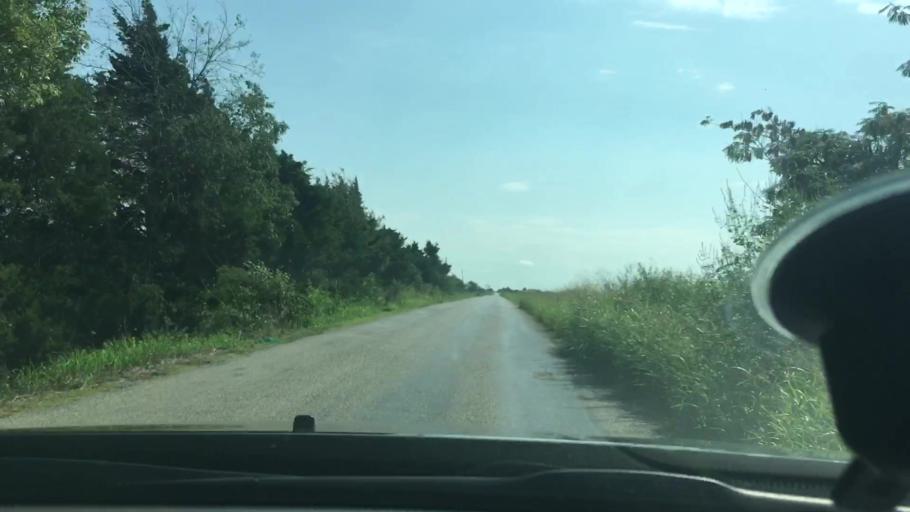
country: US
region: Oklahoma
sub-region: Bryan County
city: Colbert
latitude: 33.9110
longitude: -96.5146
